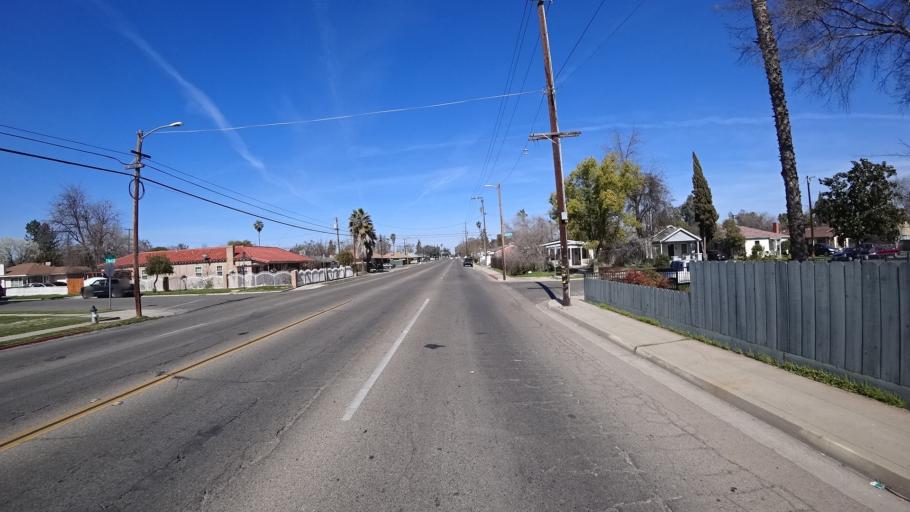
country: US
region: California
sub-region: Fresno County
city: Fresno
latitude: 36.7827
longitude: -119.8086
